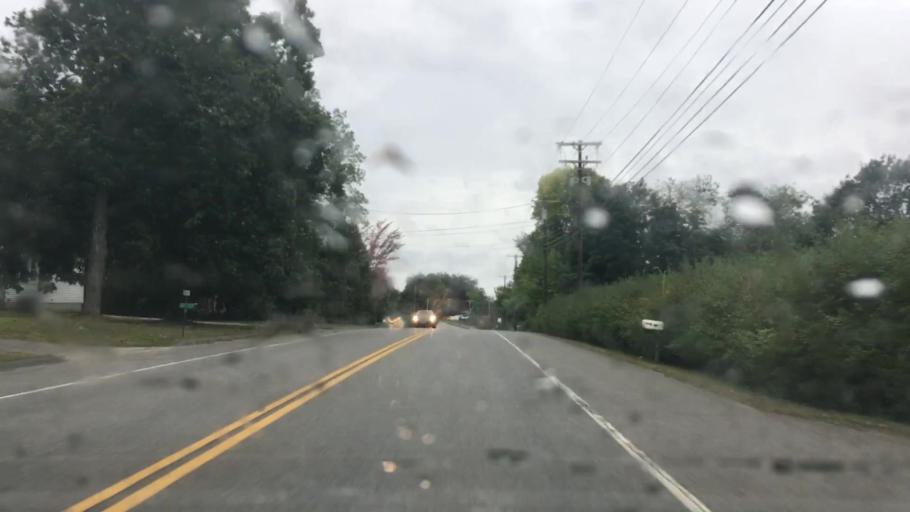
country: US
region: Maine
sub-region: Penobscot County
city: Orrington
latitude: 44.7273
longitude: -68.8272
